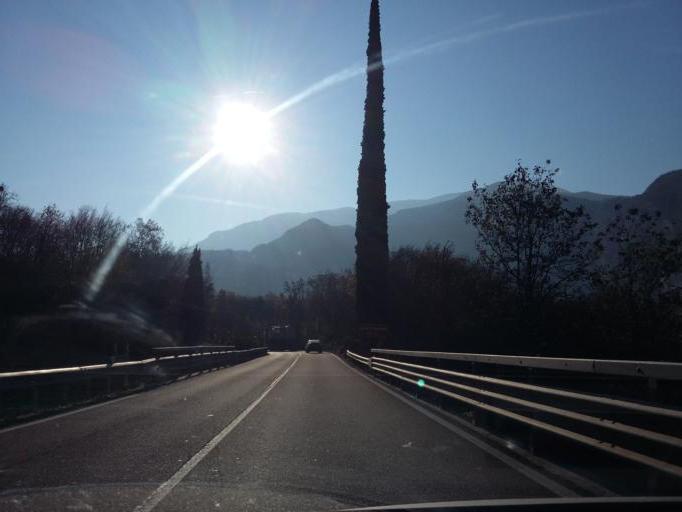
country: IT
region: Trentino-Alto Adige
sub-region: Provincia di Trento
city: Nago-Torbole
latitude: 45.8755
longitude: 10.9052
